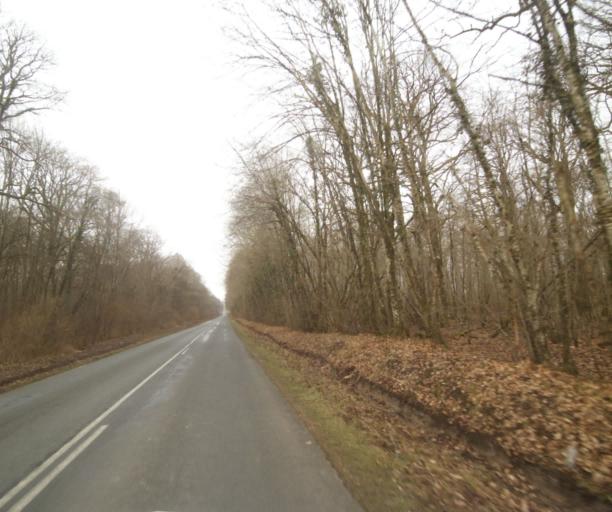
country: FR
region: Champagne-Ardenne
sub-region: Departement de la Haute-Marne
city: Villiers-en-Lieu
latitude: 48.7105
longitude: 4.8881
